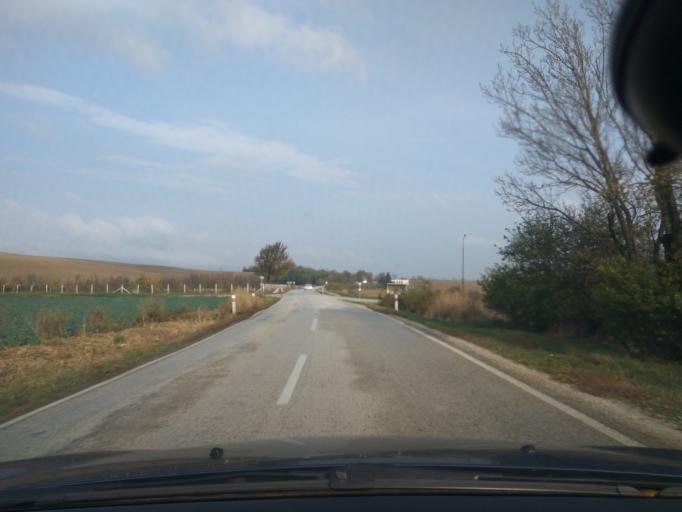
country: SK
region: Trnavsky
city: Vrbove
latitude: 48.6557
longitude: 17.7563
